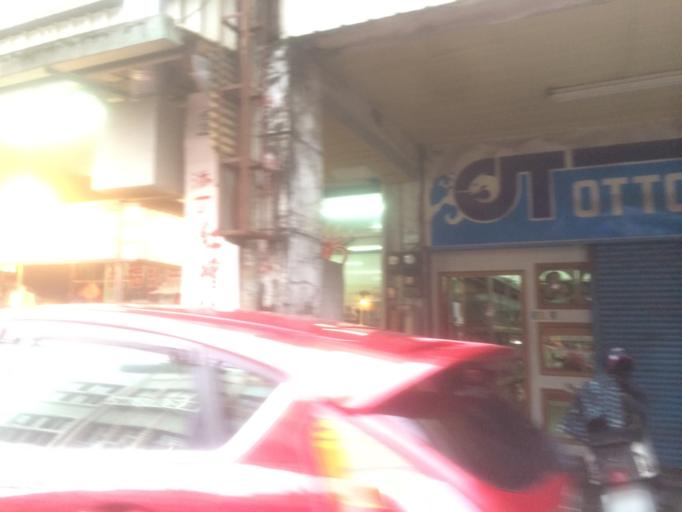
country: TW
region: Taiwan
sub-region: Yilan
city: Yilan
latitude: 24.6750
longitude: 121.7702
